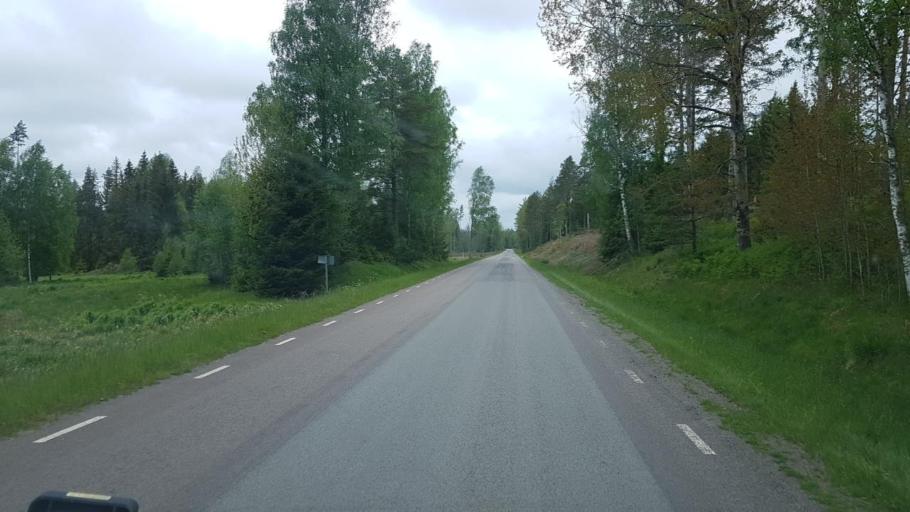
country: SE
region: OEstergoetland
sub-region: Linkopings Kommun
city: Ljungsbro
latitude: 58.5996
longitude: 15.4916
